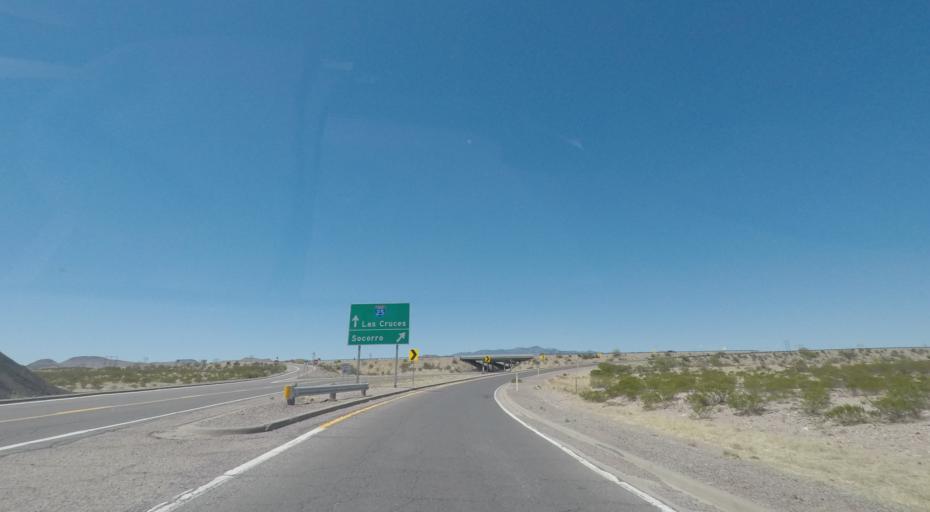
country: US
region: New Mexico
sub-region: Socorro County
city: Socorro
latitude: 33.9173
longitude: -106.8764
